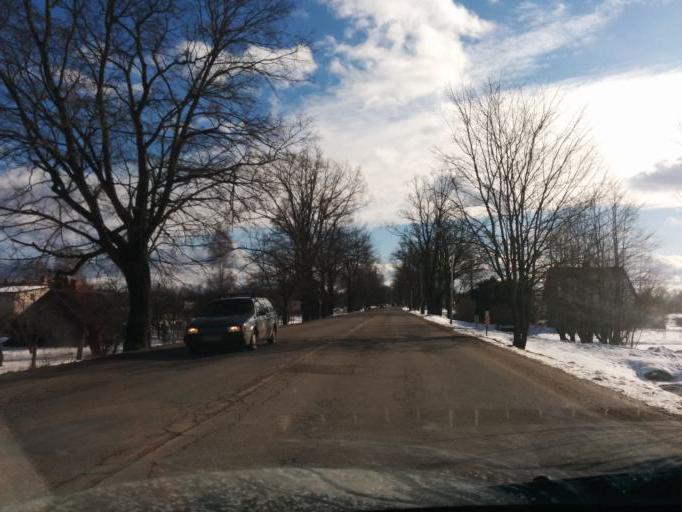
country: LV
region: Gulbenes Rajons
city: Gulbene
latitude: 57.1711
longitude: 26.7498
